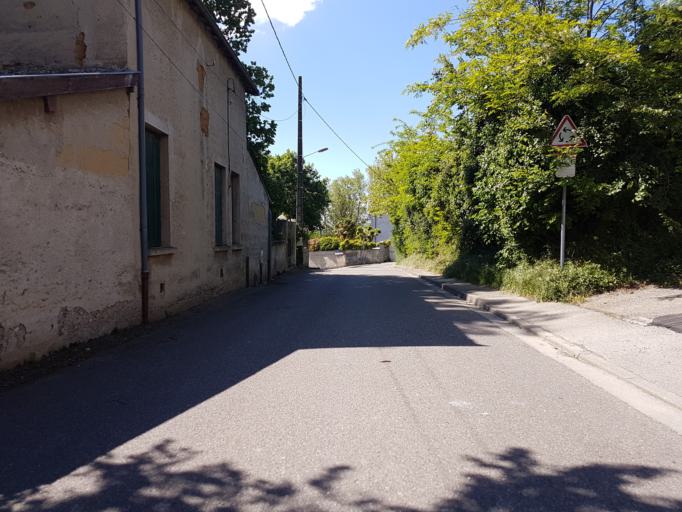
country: FR
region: Rhone-Alpes
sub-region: Departement du Rhone
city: Jonage
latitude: 45.7974
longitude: 5.0421
